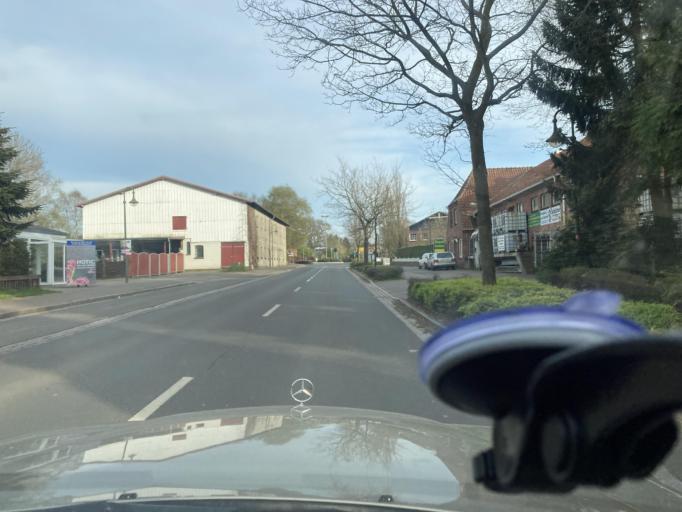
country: DE
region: Schleswig-Holstein
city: Weddingstedt
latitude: 54.2390
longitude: 9.0853
